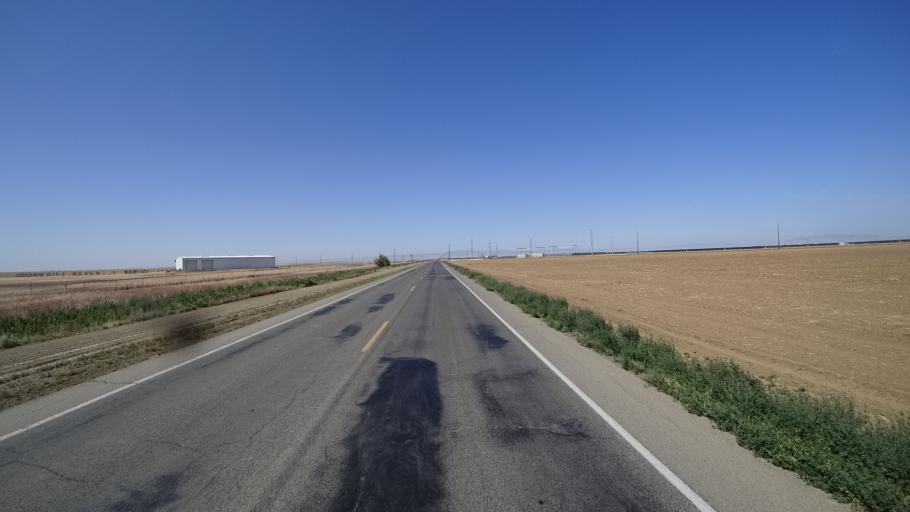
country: US
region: California
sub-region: Kings County
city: Lemoore Station
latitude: 36.2235
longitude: -119.9017
